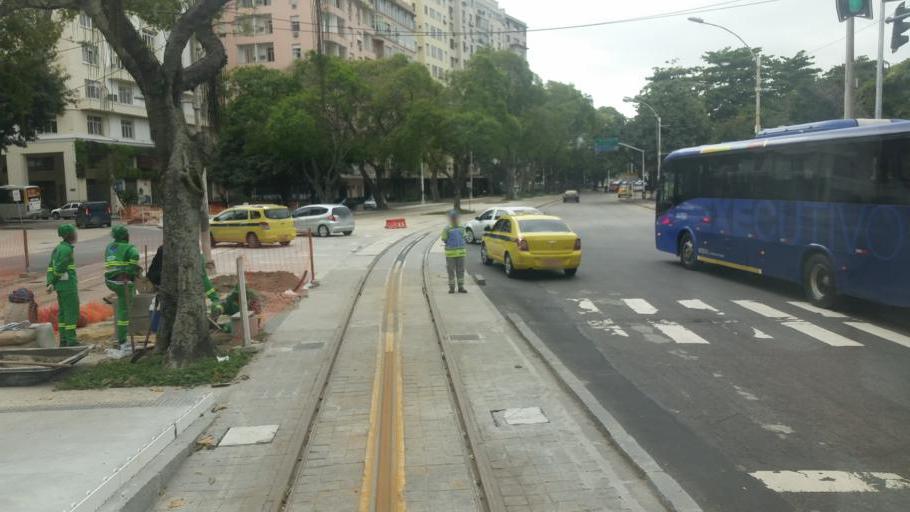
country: BR
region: Rio de Janeiro
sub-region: Rio De Janeiro
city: Rio de Janeiro
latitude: -22.9113
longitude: -43.1720
